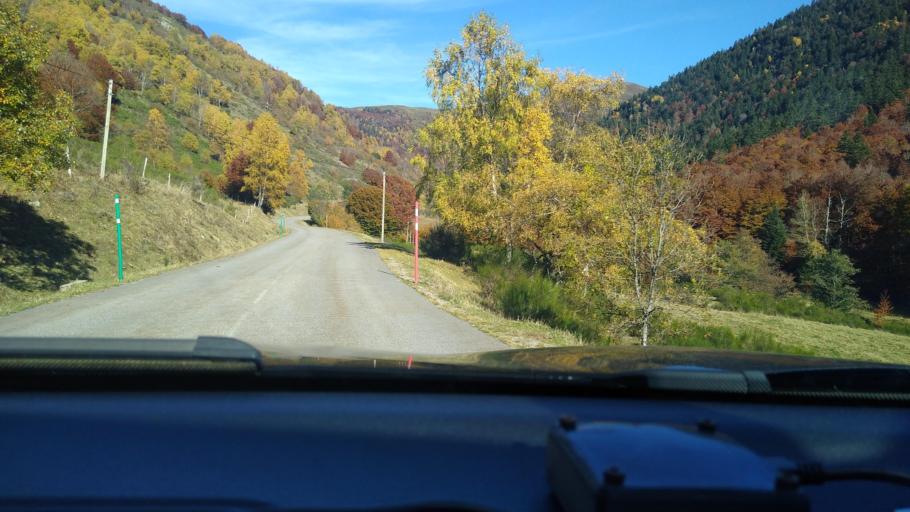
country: FR
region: Midi-Pyrenees
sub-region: Departement de l'Ariege
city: Ax-les-Thermes
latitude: 42.7236
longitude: 1.9385
